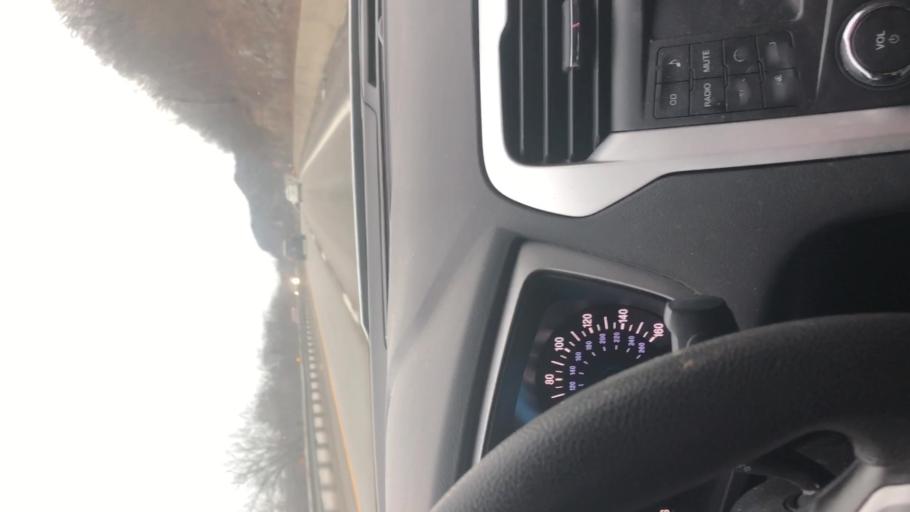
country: US
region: Kentucky
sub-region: Boyd County
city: Ashland
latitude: 38.4740
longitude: -82.6106
